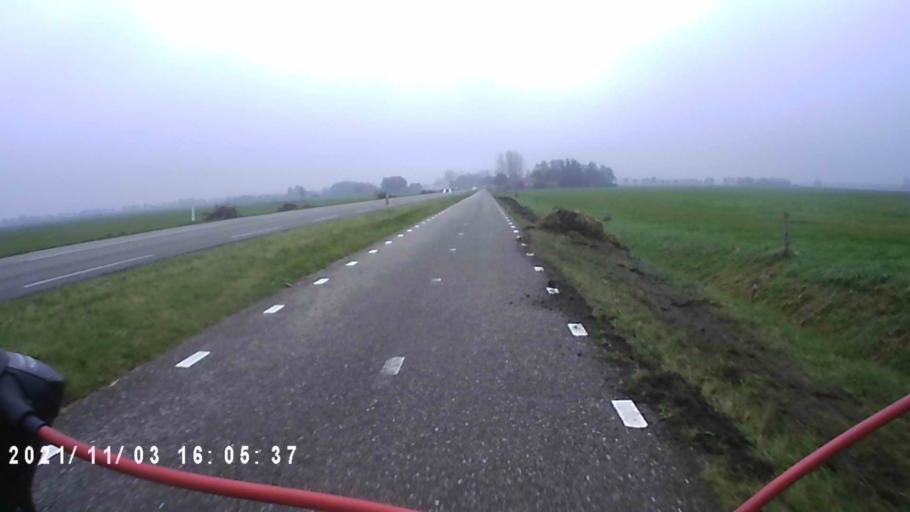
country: NL
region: Groningen
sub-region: Gemeente Leek
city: Leek
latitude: 53.0314
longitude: 6.3295
